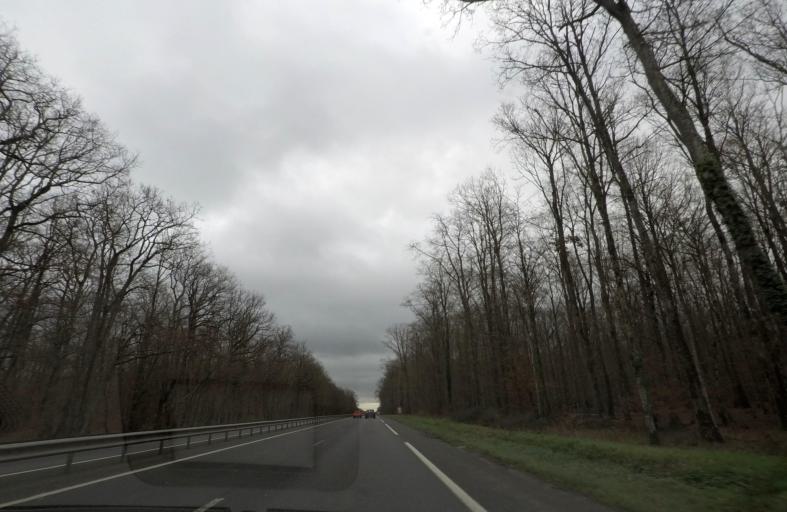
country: FR
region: Centre
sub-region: Departement du Loir-et-Cher
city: Cellettes
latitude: 47.5488
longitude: 1.3926
